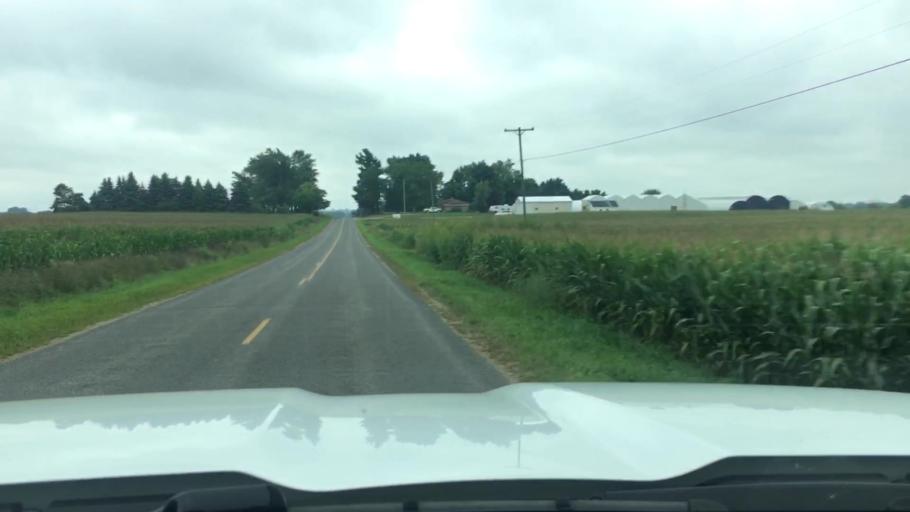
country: US
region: Michigan
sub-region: Ottawa County
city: Hudsonville
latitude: 42.7886
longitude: -85.8616
